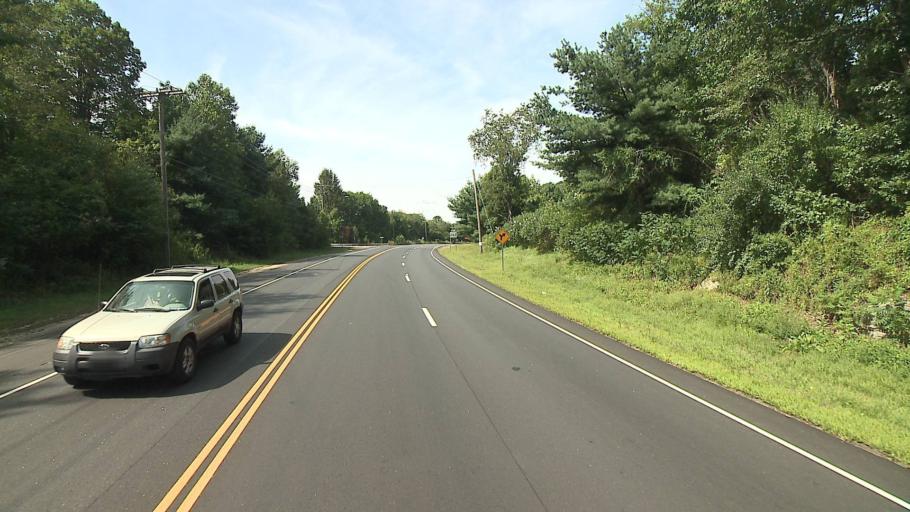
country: US
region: Connecticut
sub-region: Litchfield County
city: Oakville
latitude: 41.6031
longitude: -73.0681
